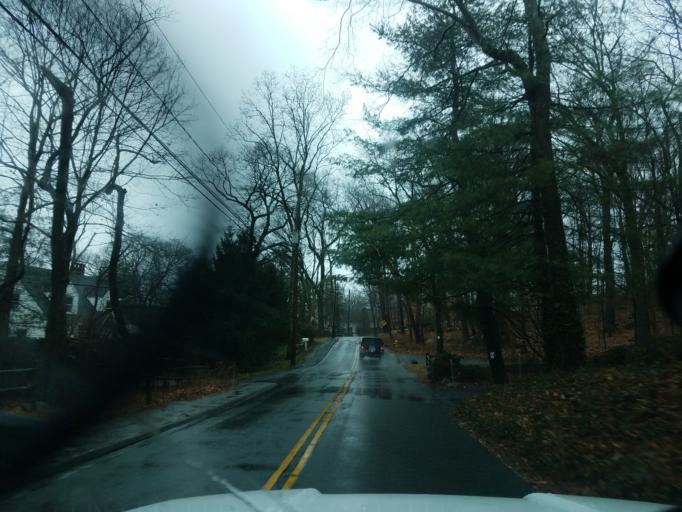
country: US
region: Connecticut
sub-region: Fairfield County
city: Darien
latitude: 41.0964
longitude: -73.4554
